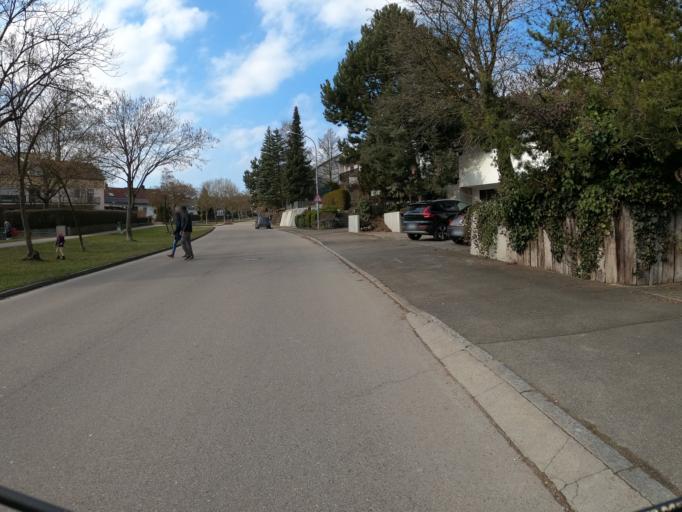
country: DE
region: Baden-Wuerttemberg
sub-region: Tuebingen Region
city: Bernstadt
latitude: 48.4433
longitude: 10.0499
